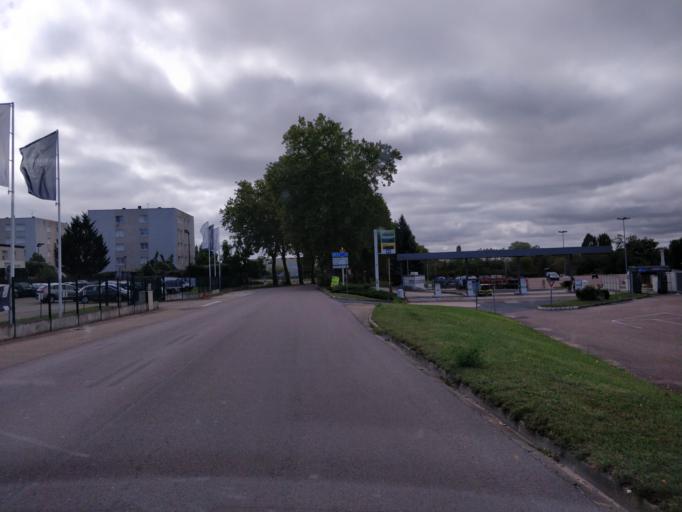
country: FR
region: Bourgogne
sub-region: Departement de l'Yonne
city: Saint-Florentin
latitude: 48.0006
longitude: 3.7197
